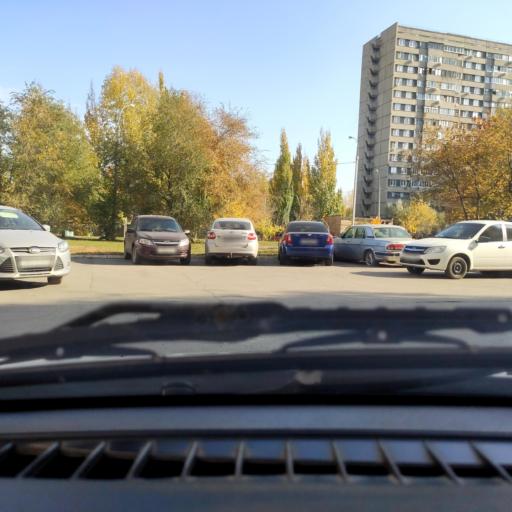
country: RU
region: Samara
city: Tol'yatti
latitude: 53.5086
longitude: 49.4442
